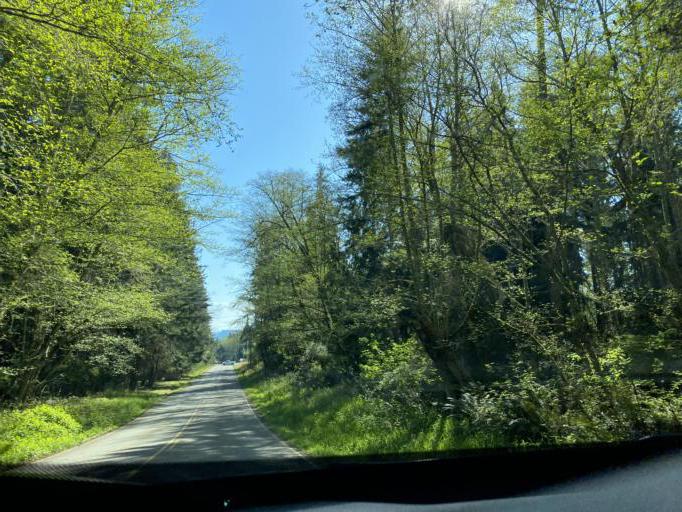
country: US
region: Washington
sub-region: Island County
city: Freeland
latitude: 48.0873
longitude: -122.5723
